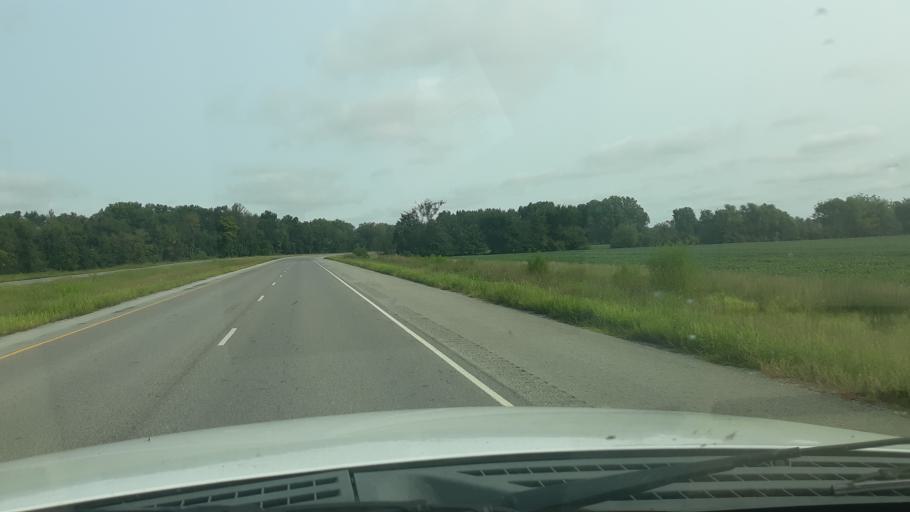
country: US
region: Illinois
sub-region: Saline County
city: Eldorado
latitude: 37.8198
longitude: -88.4269
